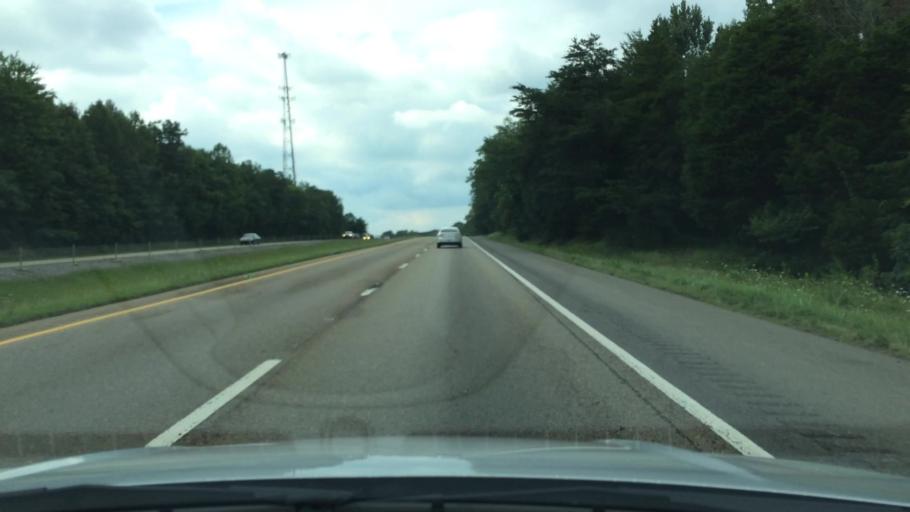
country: US
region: Tennessee
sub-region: Jefferson County
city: White Pine
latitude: 36.0144
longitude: -83.2949
